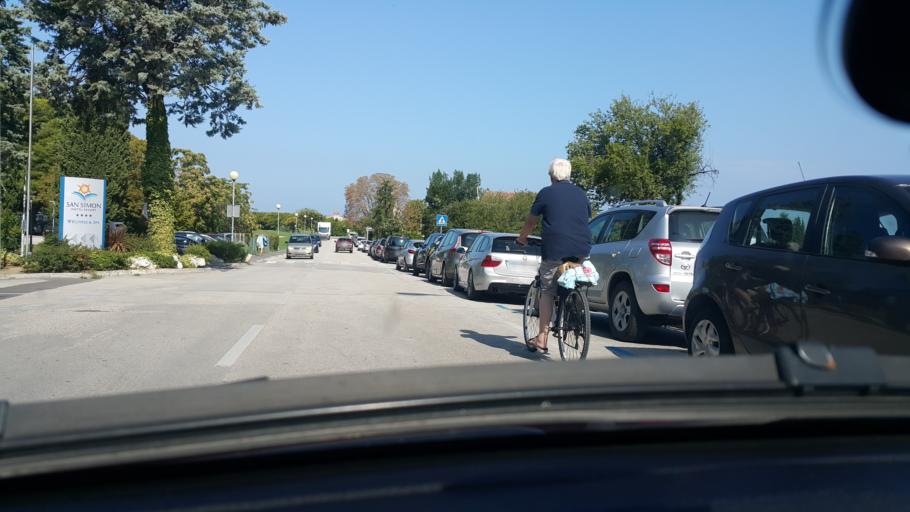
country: SI
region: Izola-Isola
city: Jagodje
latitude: 45.5308
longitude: 13.6499
